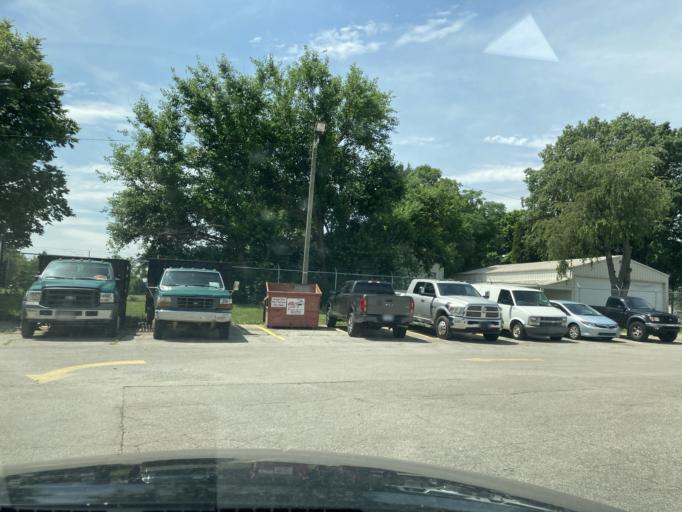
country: US
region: Indiana
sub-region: Marion County
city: Speedway
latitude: 39.8752
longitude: -86.2393
